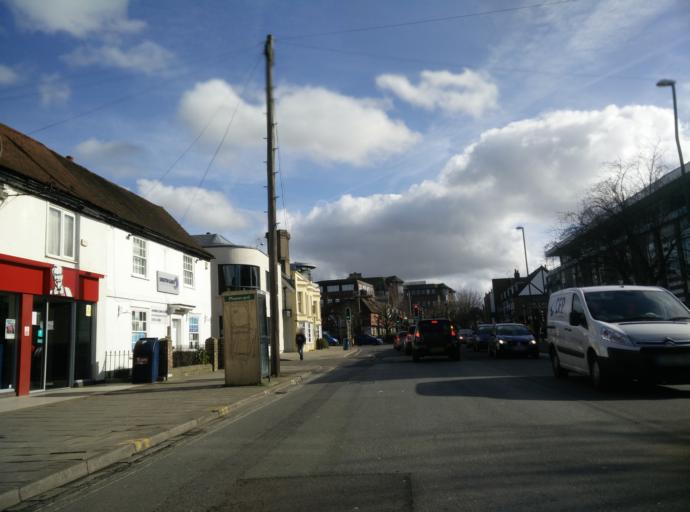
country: GB
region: England
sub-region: West Sussex
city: Horsham
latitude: 51.0642
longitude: -0.3342
